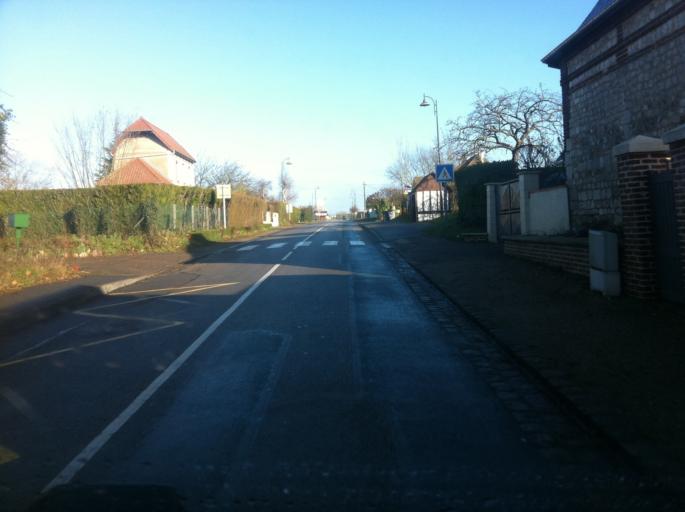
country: FR
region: Haute-Normandie
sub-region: Departement de la Seine-Maritime
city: Jumieges
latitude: 49.4366
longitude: 0.8226
